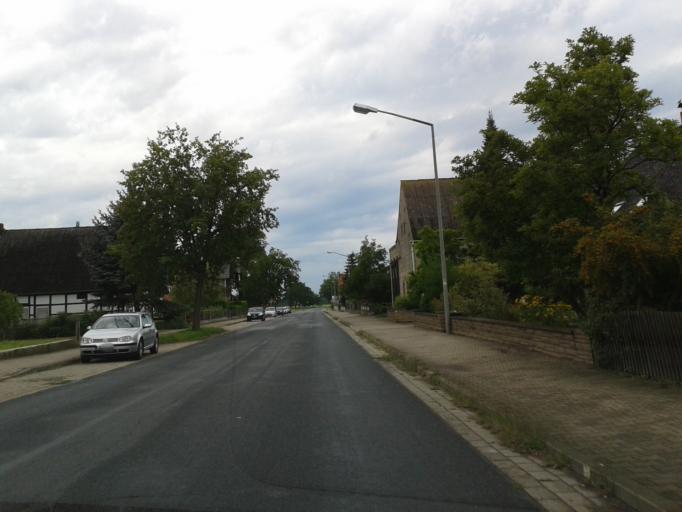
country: DE
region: Lower Saxony
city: Woltersdorf
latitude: 52.9545
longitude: 11.2189
